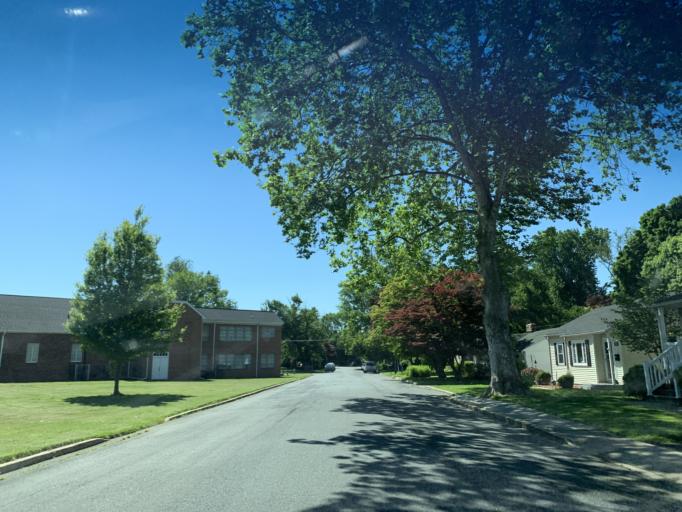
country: US
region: Maryland
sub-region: Harford County
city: Havre de Grace
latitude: 39.5394
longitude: -76.0978
